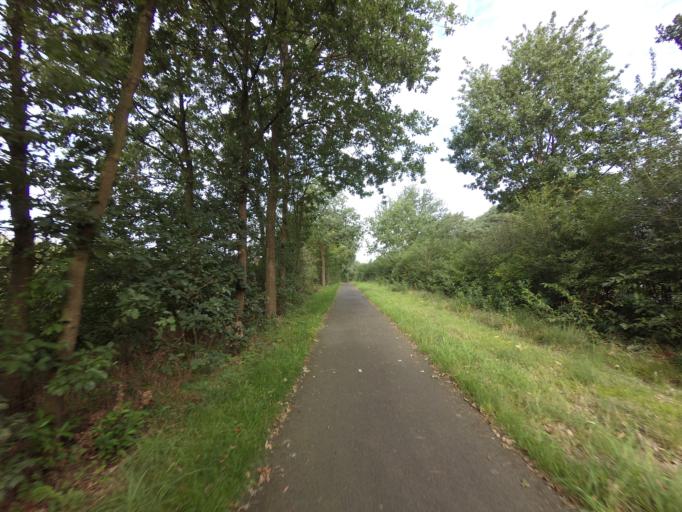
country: DE
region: Lower Saxony
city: Itterbeck
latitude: 52.5138
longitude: 6.7723
